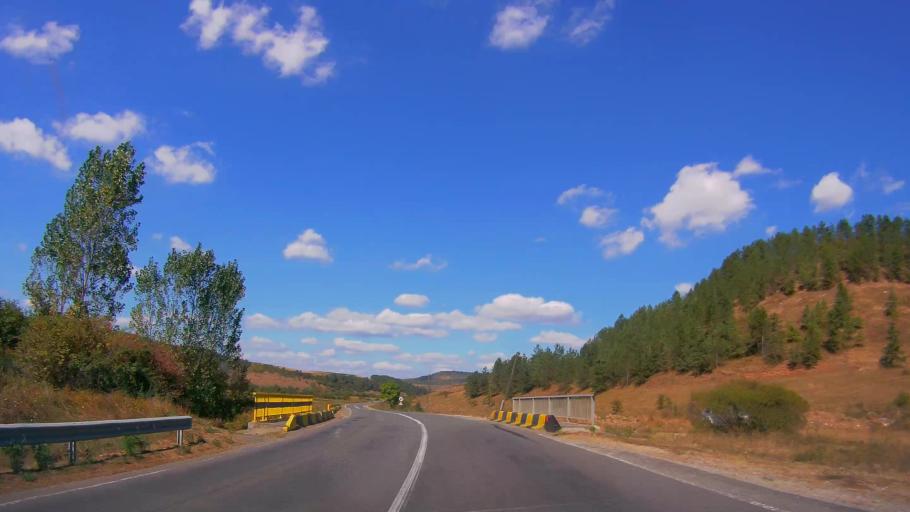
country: RO
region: Cluj
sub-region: Comuna Sanpaul
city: Sanpaul
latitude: 46.8366
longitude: 23.4074
